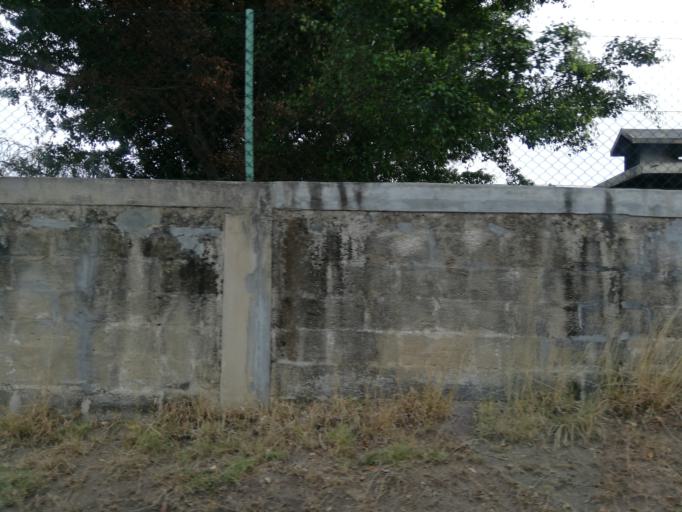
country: MU
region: Black River
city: Petite Riviere
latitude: -20.2094
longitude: 57.4666
